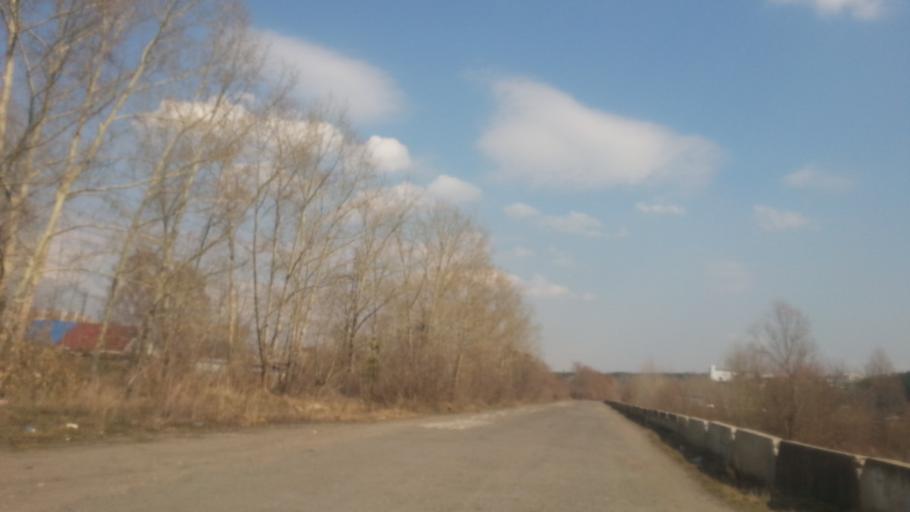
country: RU
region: Altai Krai
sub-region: Gorod Barnaulskiy
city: Barnaul
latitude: 53.3116
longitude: 83.7276
